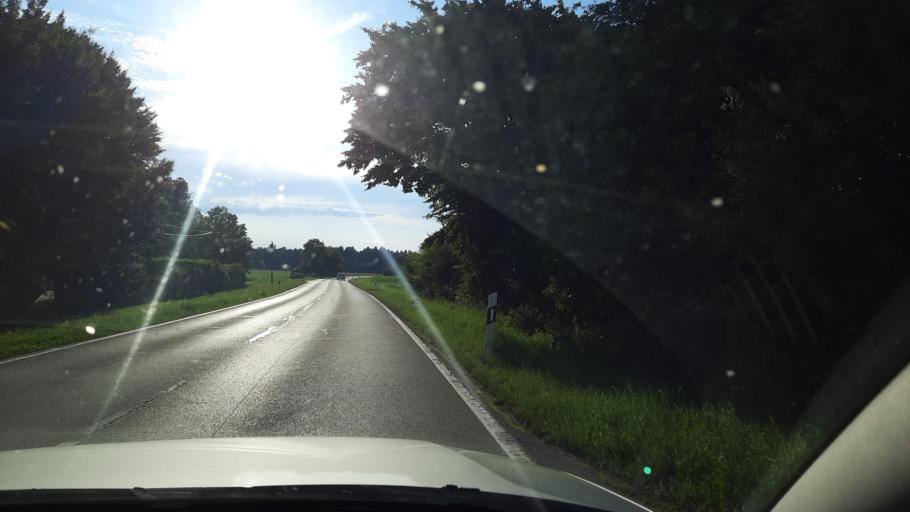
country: DE
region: Bavaria
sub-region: Upper Bavaria
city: Oberpframmern
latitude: 48.0260
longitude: 11.8022
